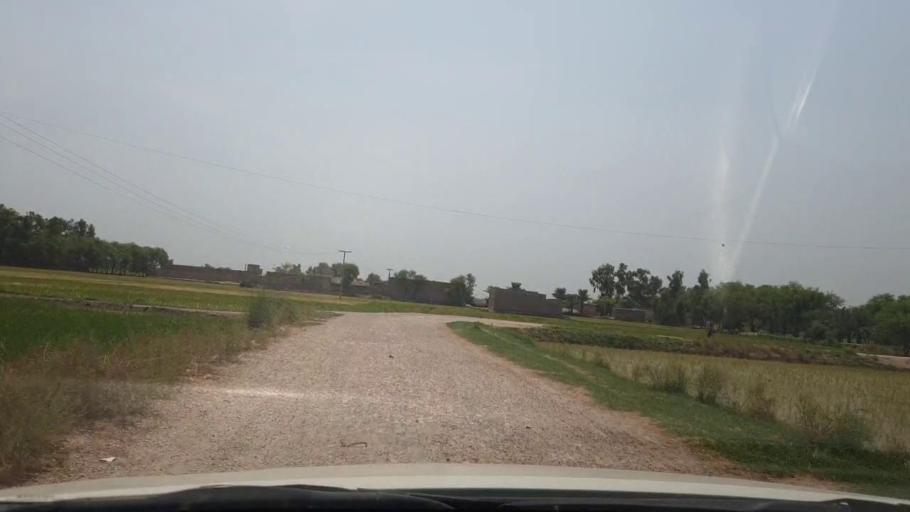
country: PK
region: Sindh
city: Rustam jo Goth
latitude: 28.0069
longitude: 68.7688
